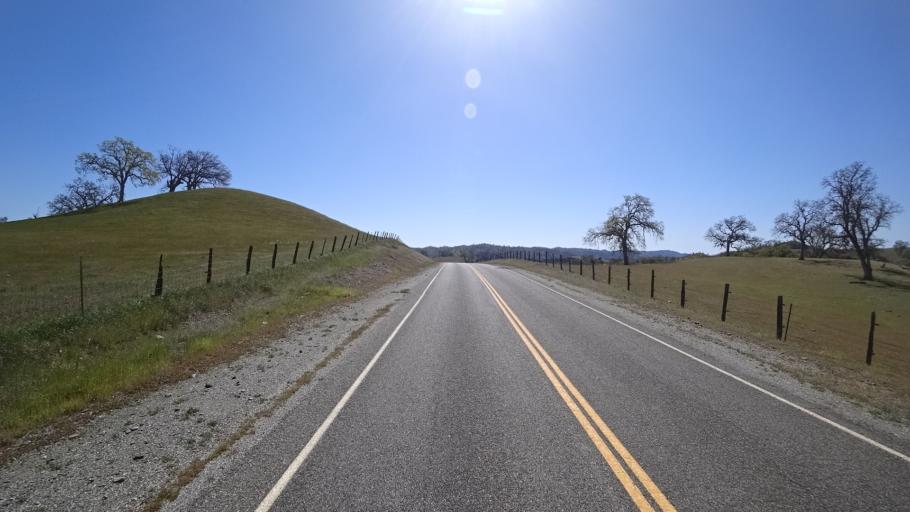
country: US
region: California
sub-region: Glenn County
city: Orland
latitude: 39.6867
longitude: -122.5413
